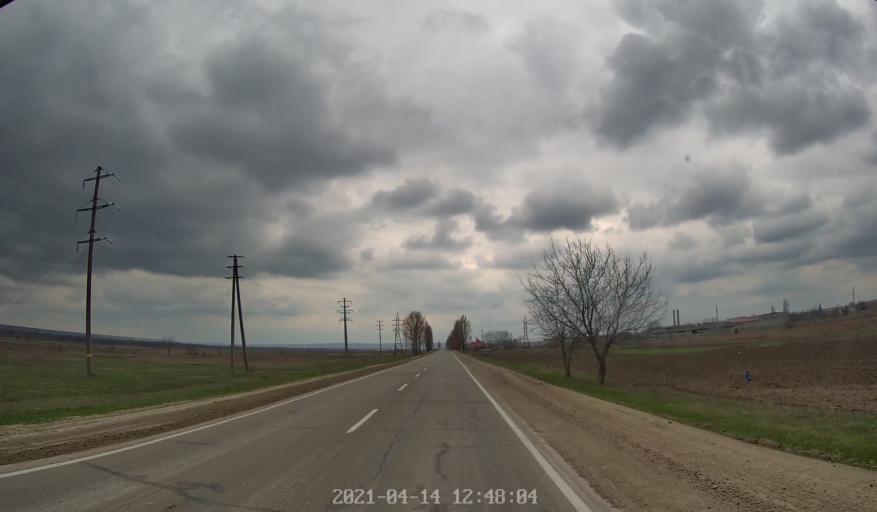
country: MD
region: Criuleni
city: Criuleni
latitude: 47.1555
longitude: 29.1576
